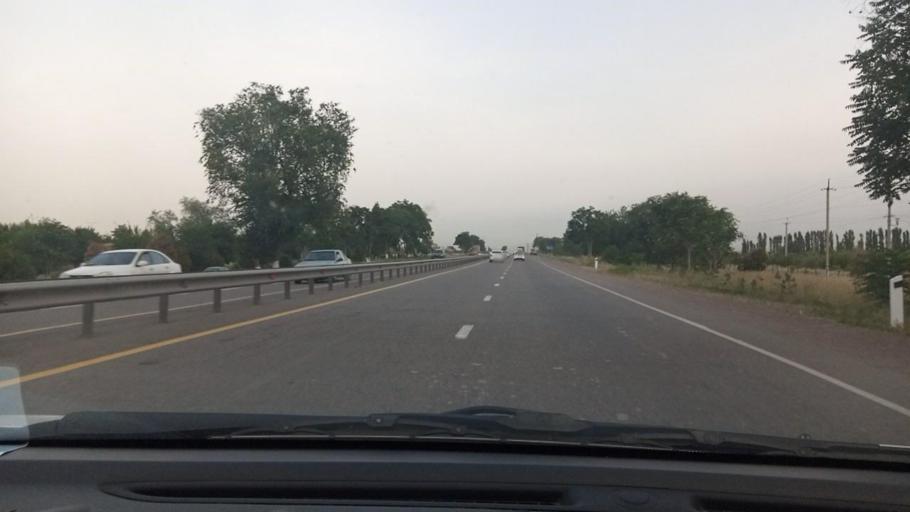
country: UZ
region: Toshkent
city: Ohangaron
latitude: 40.9357
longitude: 69.5881
